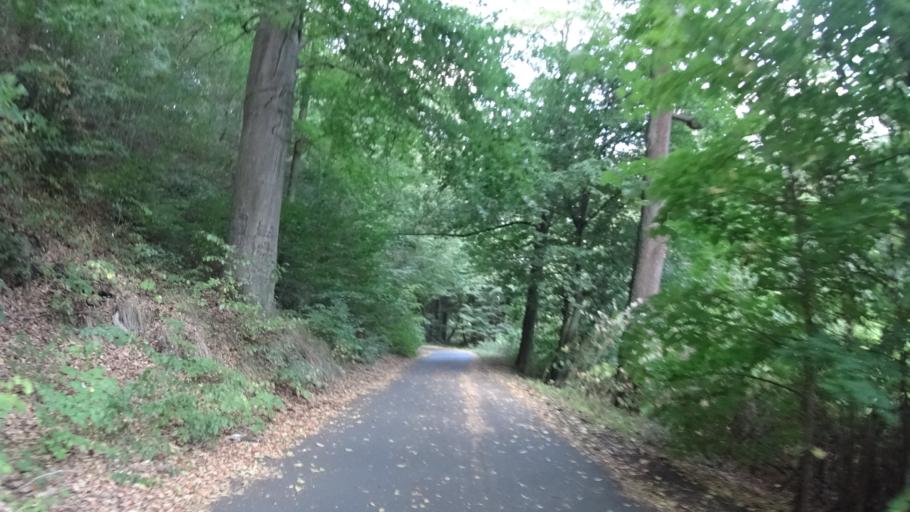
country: DE
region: Saxony
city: Schlegel
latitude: 50.9721
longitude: 14.9042
